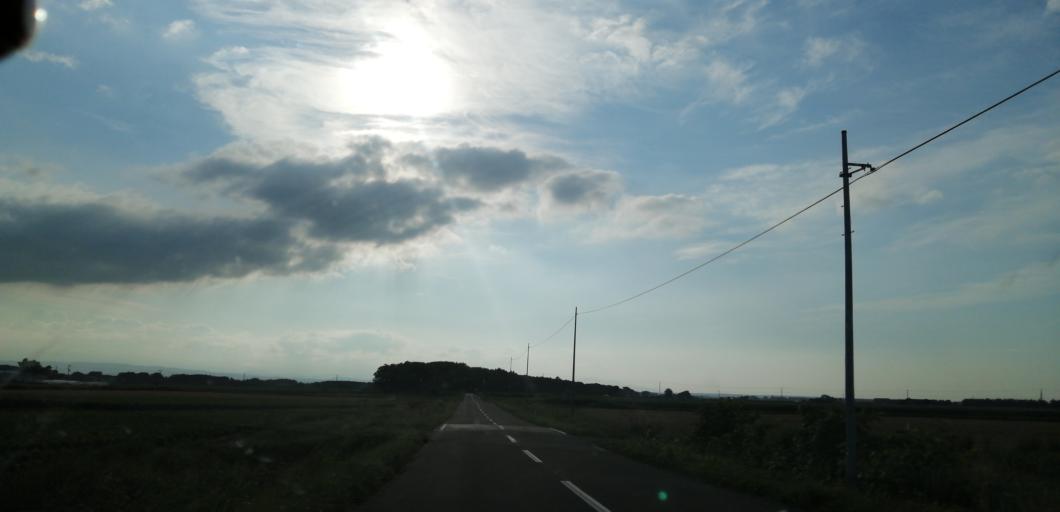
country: JP
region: Hokkaido
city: Chitose
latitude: 42.9366
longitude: 141.7104
